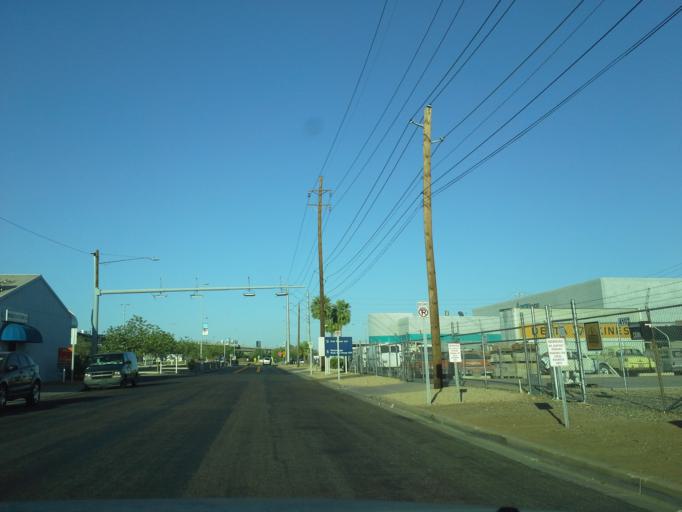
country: US
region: Arizona
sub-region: Maricopa County
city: Tempe Junction
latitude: 33.4462
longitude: -111.9923
